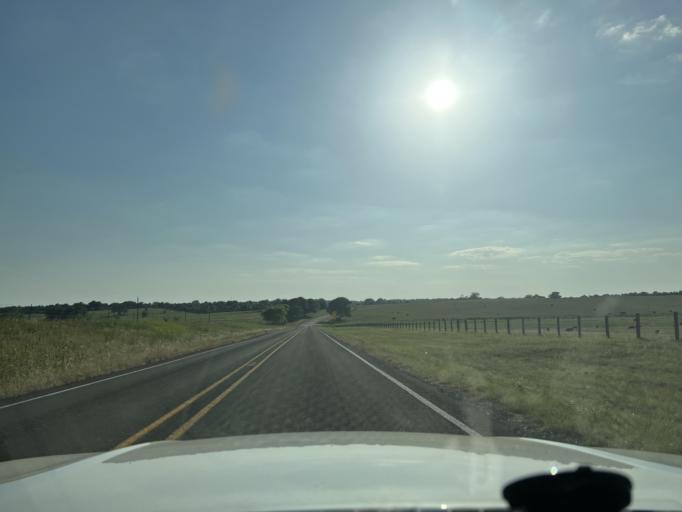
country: US
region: Texas
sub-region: Washington County
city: Brenham
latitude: 30.2406
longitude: -96.2440
